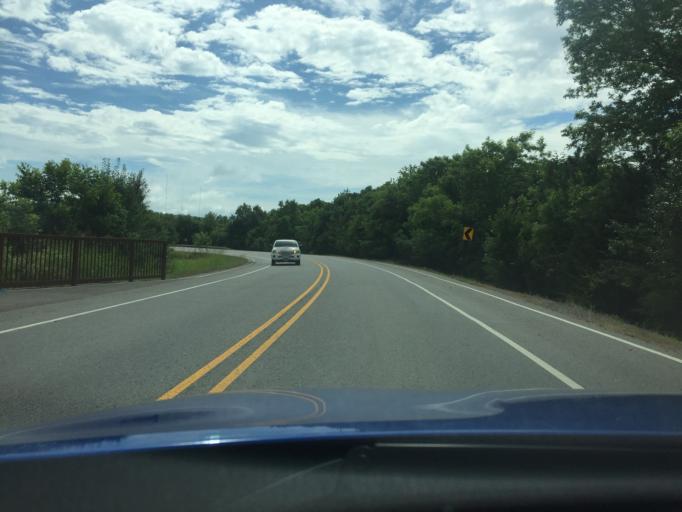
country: US
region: Arkansas
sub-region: Pulaski County
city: Maumelle
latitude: 34.8170
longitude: -92.4407
